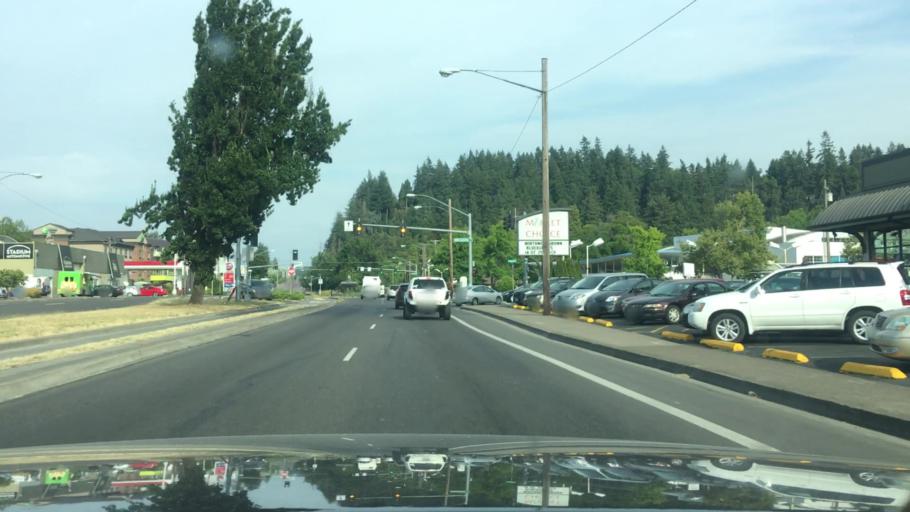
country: US
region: Oregon
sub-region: Lane County
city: Eugene
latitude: 44.0452
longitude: -123.0640
